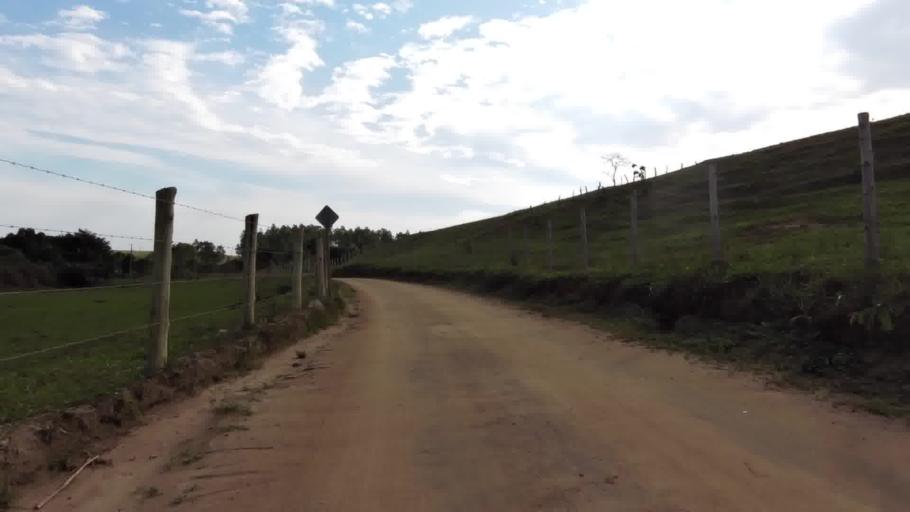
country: BR
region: Espirito Santo
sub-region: Piuma
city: Piuma
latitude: -20.8190
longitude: -40.7395
